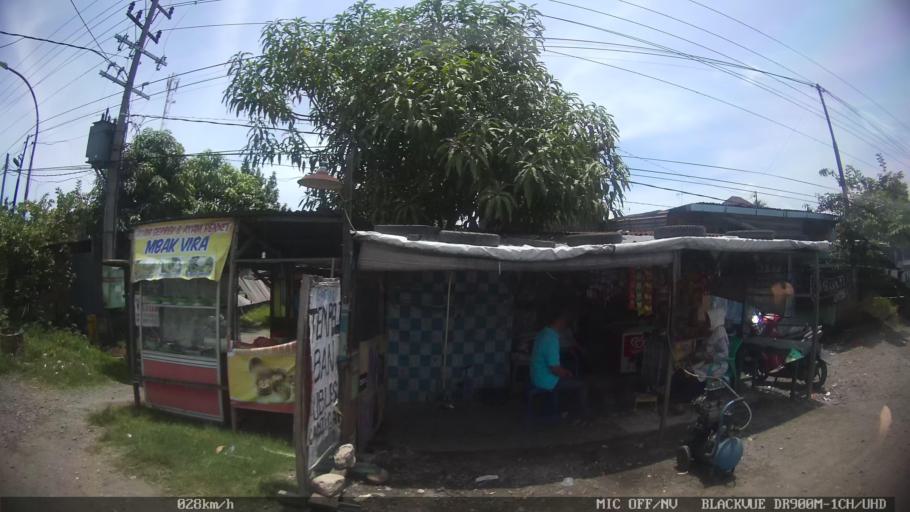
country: ID
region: North Sumatra
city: Labuhan Deli
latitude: 3.7465
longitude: 98.6744
